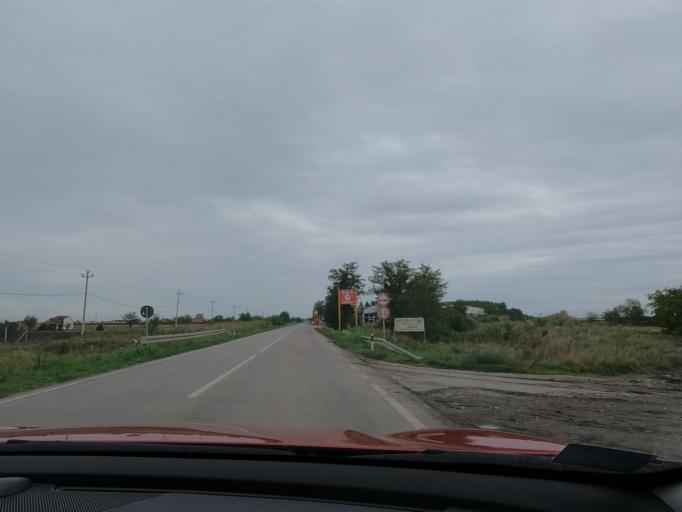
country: RS
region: Autonomna Pokrajina Vojvodina
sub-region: Severnobanatski Okrug
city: Kikinda
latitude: 45.7860
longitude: 20.4328
